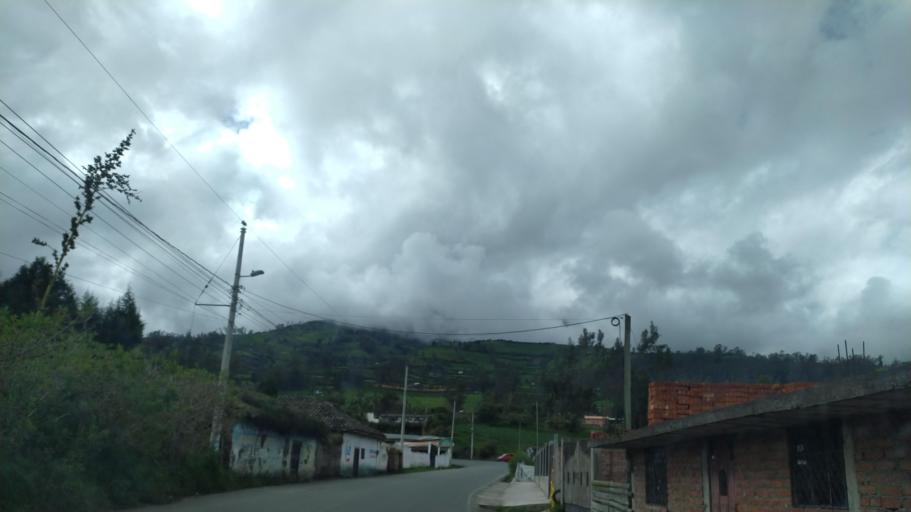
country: EC
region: Chimborazo
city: Riobamba
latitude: -1.6578
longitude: -78.5715
